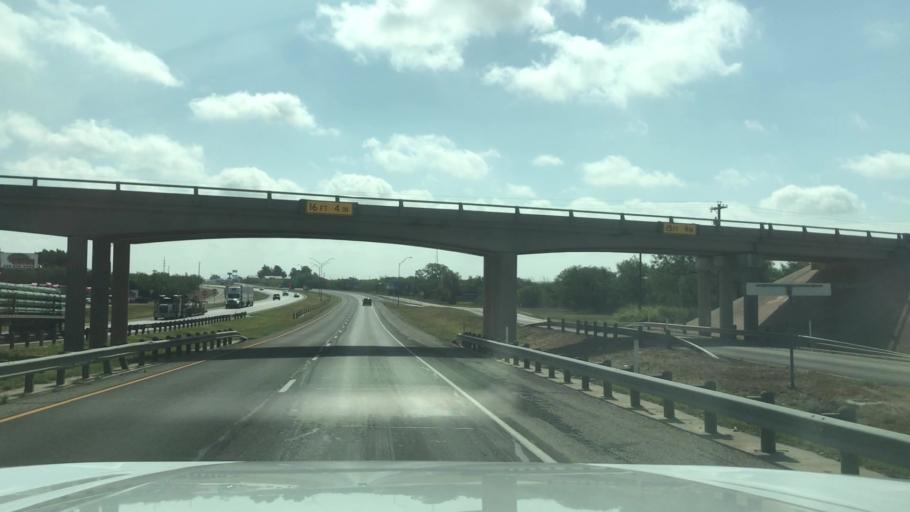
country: US
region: Texas
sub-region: Nolan County
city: Sweetwater
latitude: 32.4477
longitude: -100.4159
